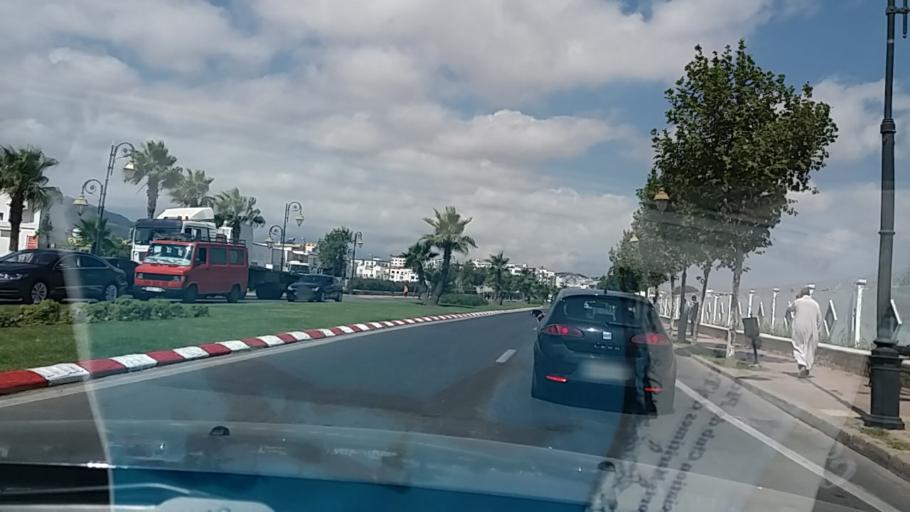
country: MA
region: Tanger-Tetouan
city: Tetouan
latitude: 35.5839
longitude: -5.3318
